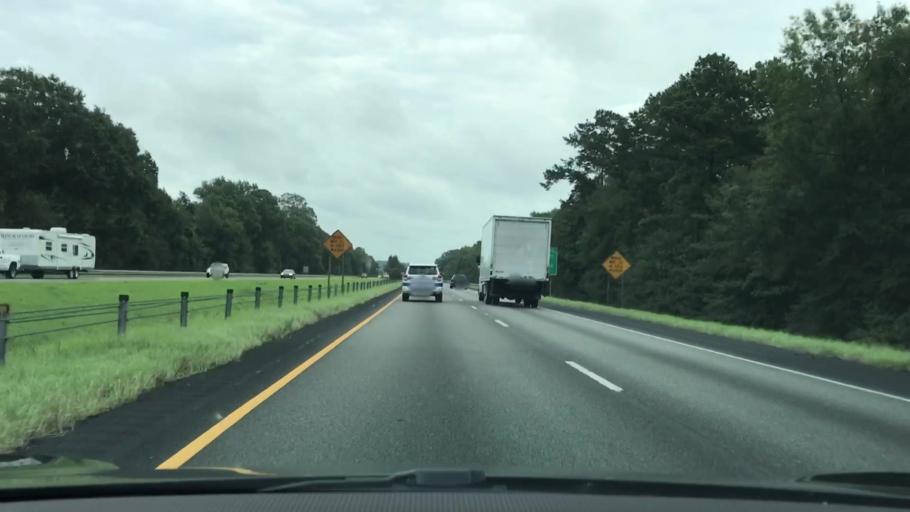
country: US
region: Alabama
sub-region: Elmore County
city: Tallassee
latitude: 32.4260
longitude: -85.9136
